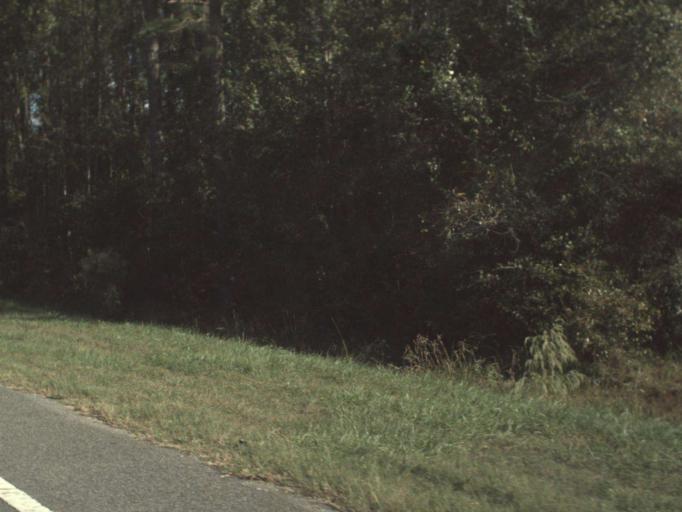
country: US
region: Florida
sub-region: Washington County
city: Chipley
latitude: 30.7814
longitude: -85.5176
